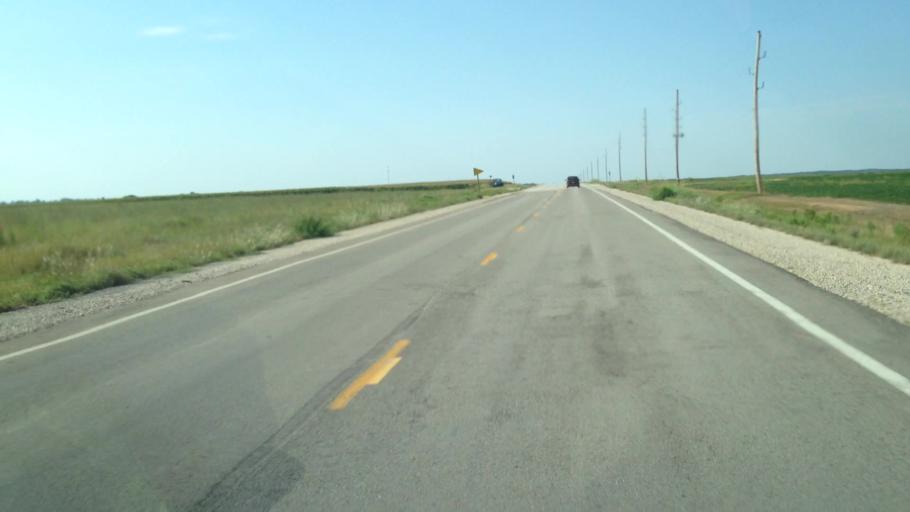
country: US
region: Kansas
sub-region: Anderson County
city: Garnett
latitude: 38.0505
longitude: -95.1695
